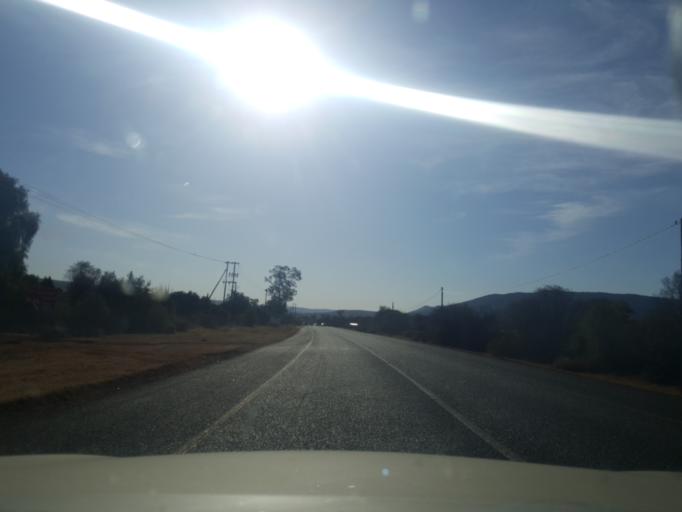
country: ZA
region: North-West
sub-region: Ngaka Modiri Molema District Municipality
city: Zeerust
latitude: -25.4537
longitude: 25.8726
